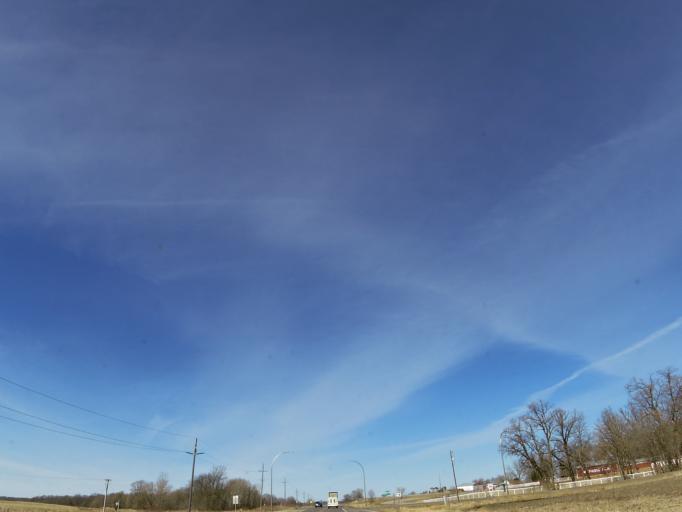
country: US
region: Minnesota
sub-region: Wright County
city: Buffalo
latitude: 45.2002
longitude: -93.9073
